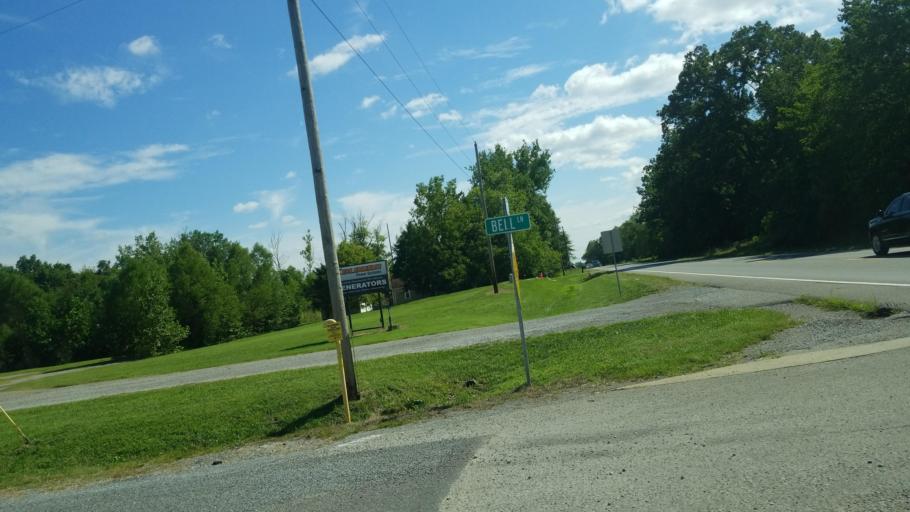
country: US
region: Illinois
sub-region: Williamson County
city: Marion
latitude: 37.7611
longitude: -88.9327
